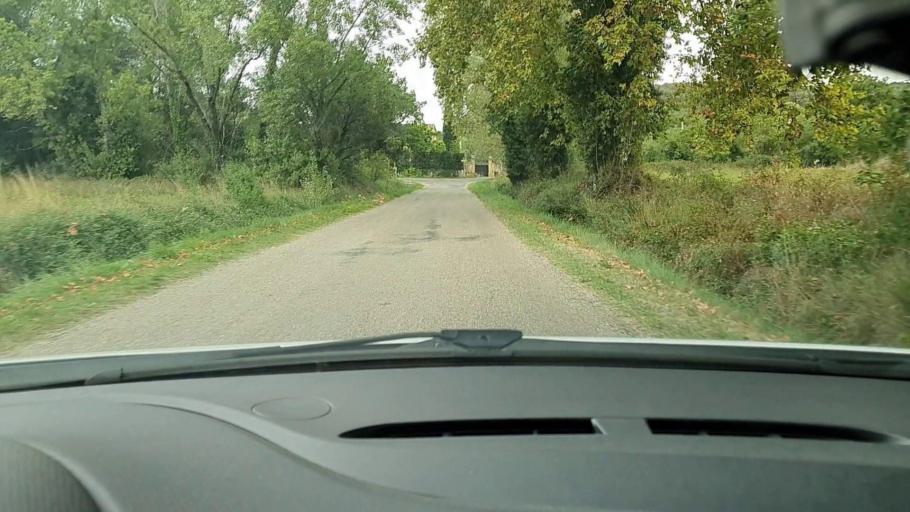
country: FR
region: Languedoc-Roussillon
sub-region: Departement du Gard
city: Montaren-et-Saint-Mediers
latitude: 44.0556
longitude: 4.3235
